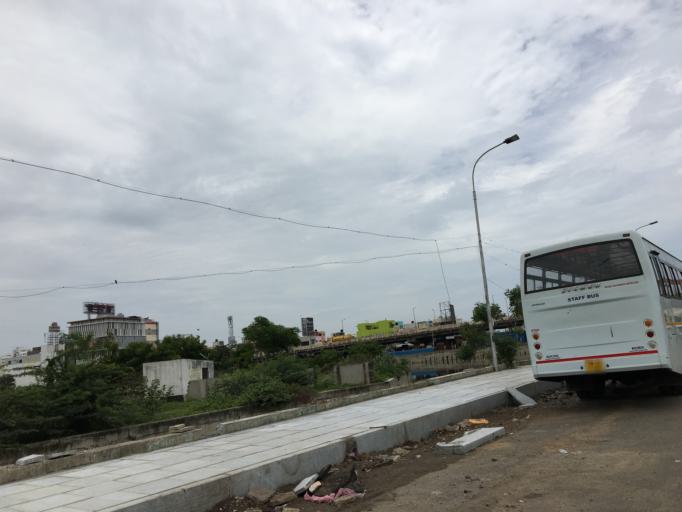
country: IN
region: Tamil Nadu
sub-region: Kancheepuram
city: Madipakkam
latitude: 12.9688
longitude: 80.2162
